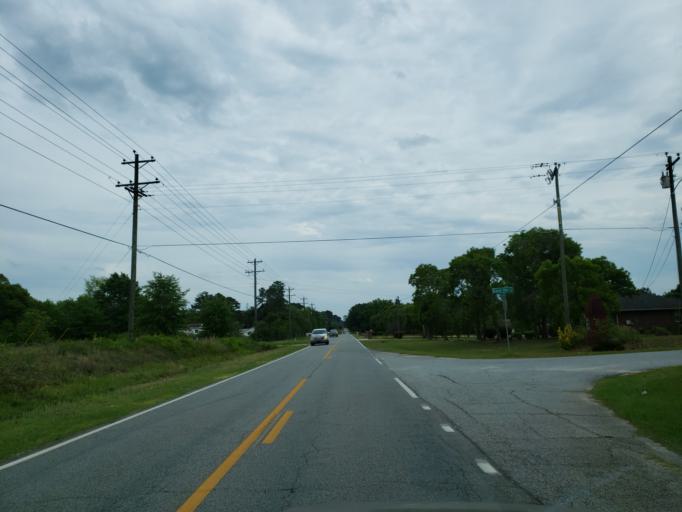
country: US
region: Georgia
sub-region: Bibb County
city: West Point
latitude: 32.7762
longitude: -83.7822
